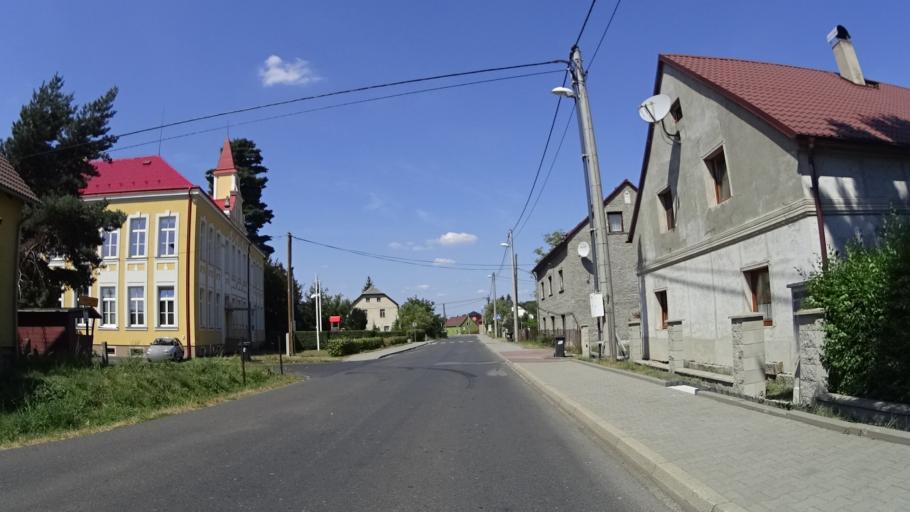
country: CZ
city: Hradek nad Nisou
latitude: 50.8469
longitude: 14.8522
